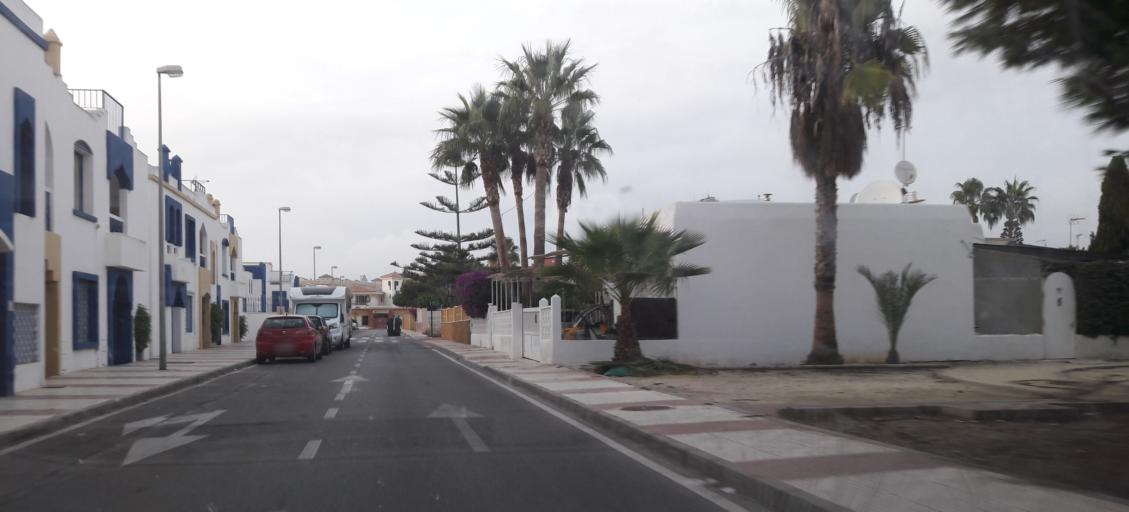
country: ES
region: Andalusia
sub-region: Provincia de Almeria
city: Roquetas de Mar
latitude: 36.7302
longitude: -2.6266
